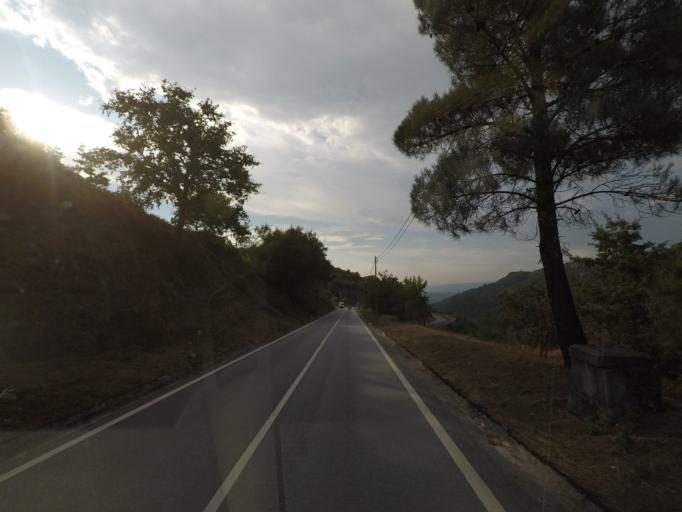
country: PT
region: Porto
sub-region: Baiao
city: Valadares
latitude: 41.2148
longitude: -7.9795
